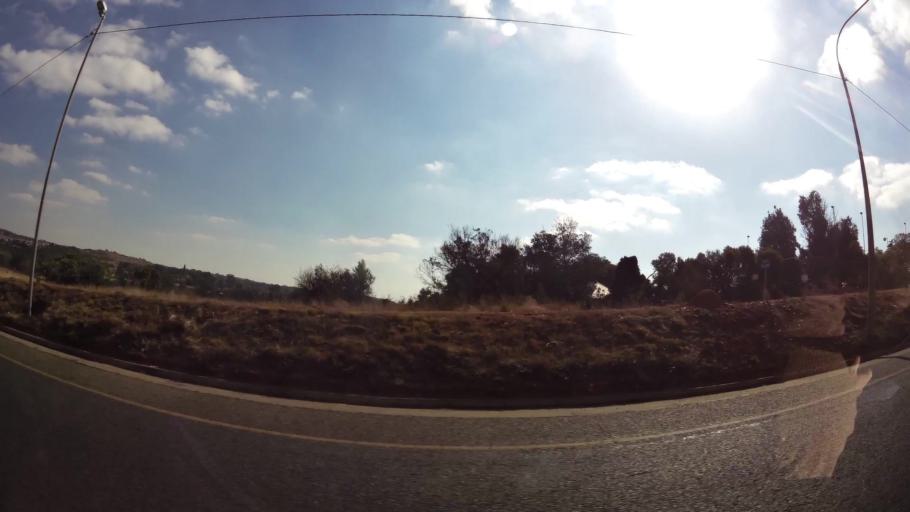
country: ZA
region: Gauteng
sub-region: West Rand District Municipality
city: Krugersdorp
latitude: -26.0671
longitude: 27.8041
